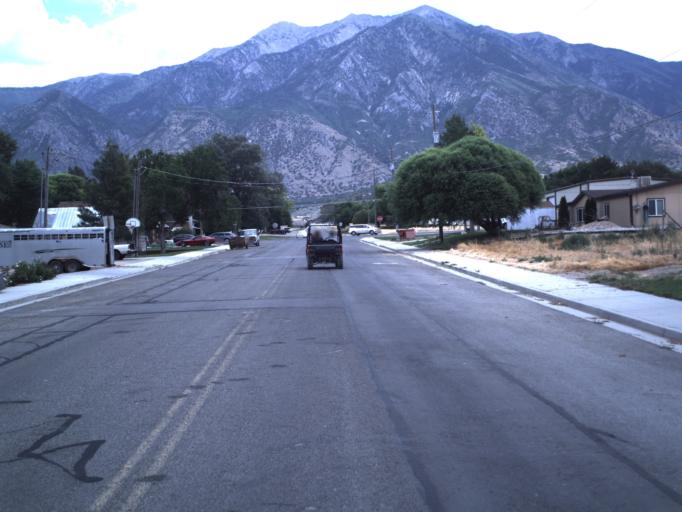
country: US
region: Utah
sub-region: Juab County
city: Mona
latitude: 39.8191
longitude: -111.8569
